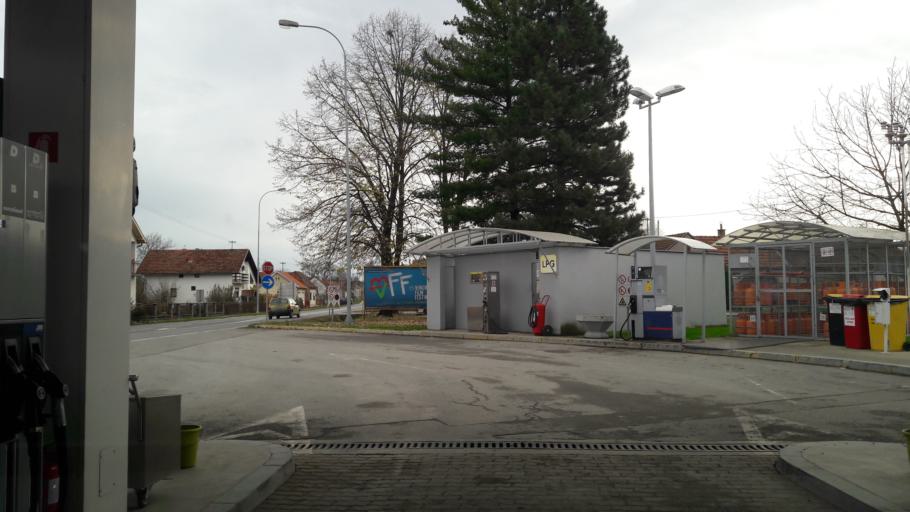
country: HR
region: Virovitick-Podravska
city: Orahovica
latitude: 45.5482
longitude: 17.9027
